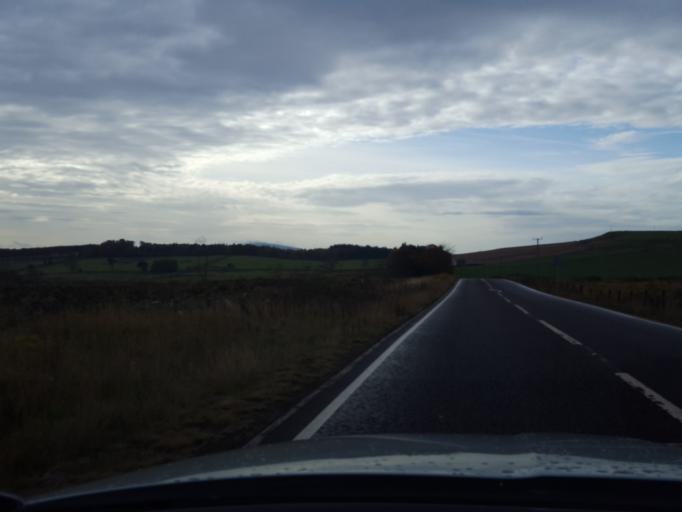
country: GB
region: Scotland
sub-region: South Lanarkshire
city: Carnwath
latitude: 55.7261
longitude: -3.5768
